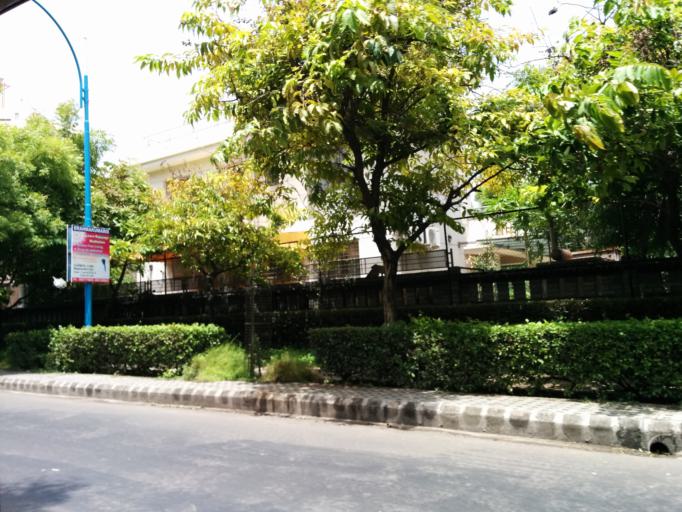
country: IN
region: Maharashtra
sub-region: Pune Division
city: Pune
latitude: 18.5138
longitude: 73.9306
